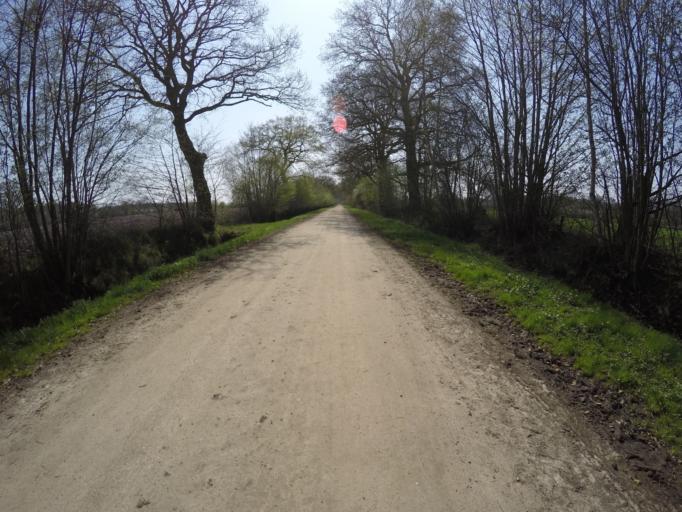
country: DE
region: Schleswig-Holstein
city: Borstel-Hohenraden
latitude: 53.7161
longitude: 9.8299
